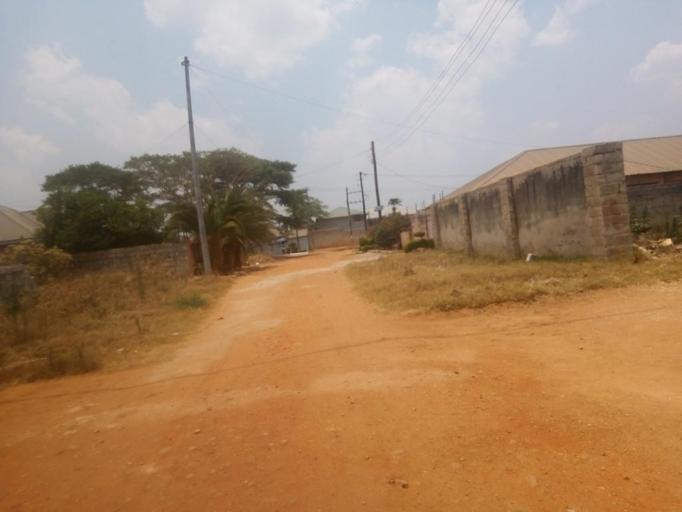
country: ZM
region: Lusaka
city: Lusaka
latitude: -15.3956
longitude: 28.3921
